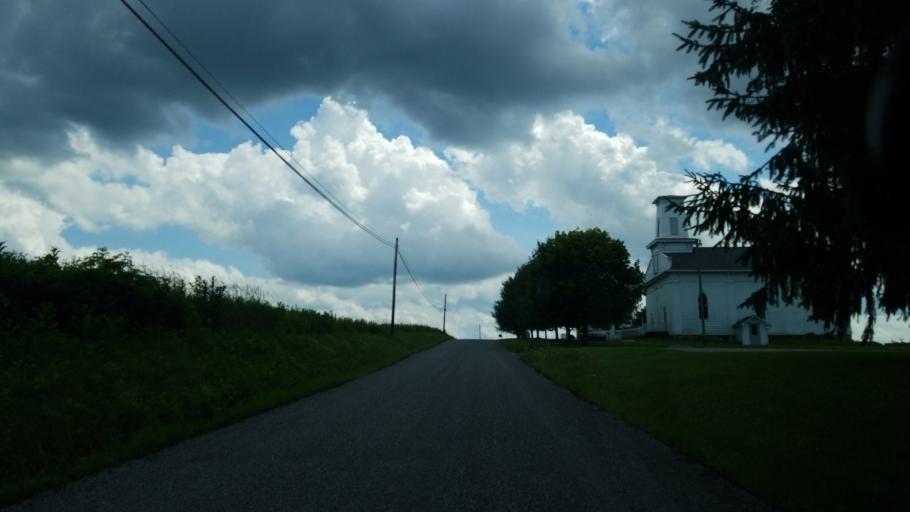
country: US
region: Pennsylvania
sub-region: Jefferson County
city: Brookville
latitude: 41.2370
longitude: -79.0116
